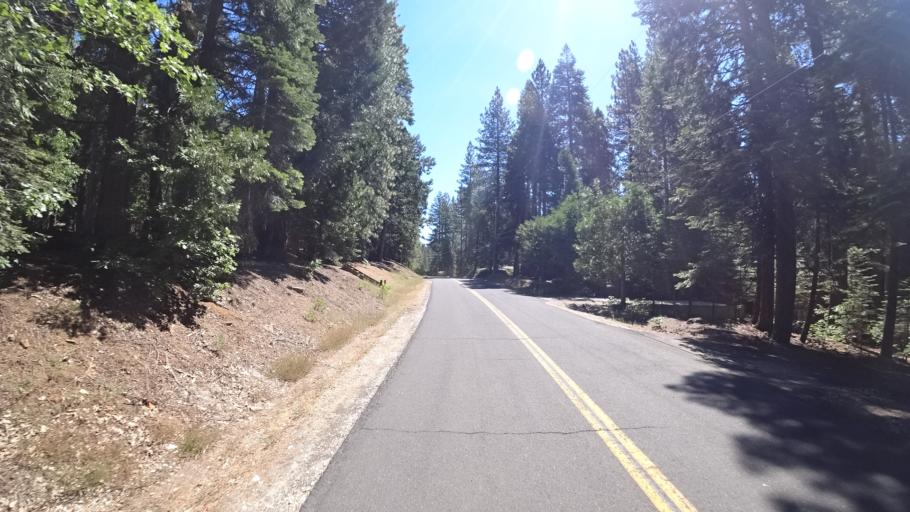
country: US
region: California
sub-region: Calaveras County
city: Arnold
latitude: 38.2971
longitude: -120.2788
